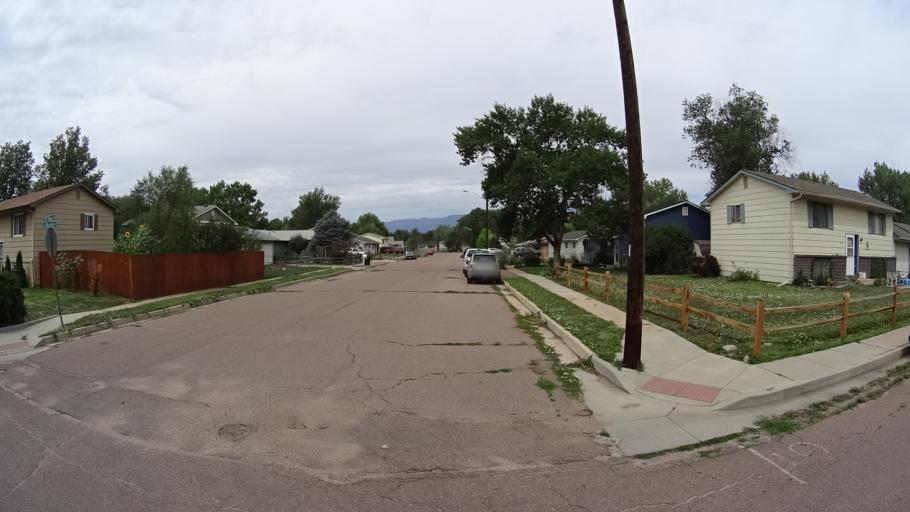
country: US
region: Colorado
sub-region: El Paso County
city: Fountain
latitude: 38.6887
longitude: -104.7013
